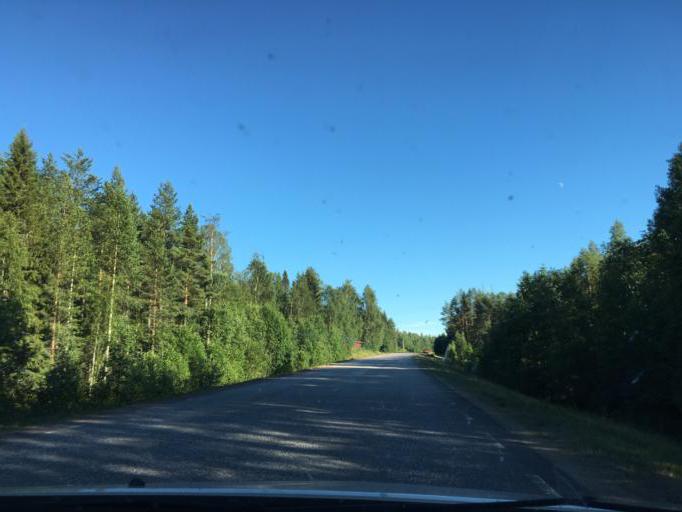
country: SE
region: Norrbotten
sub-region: Kalix Kommun
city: Rolfs
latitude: 65.9125
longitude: 22.9266
